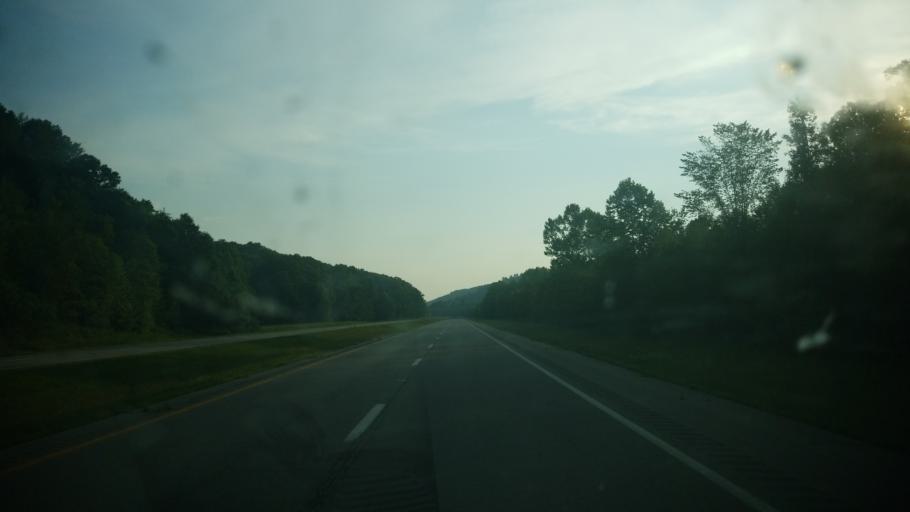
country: US
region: Ohio
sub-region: Pike County
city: Piketon
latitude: 39.0513
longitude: -83.1996
